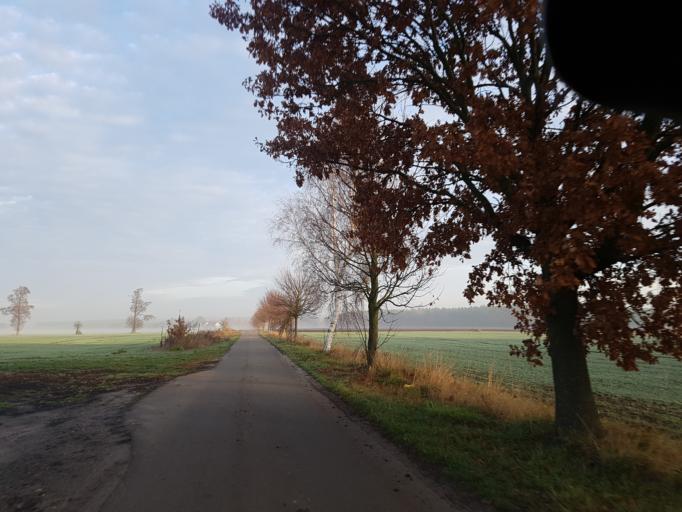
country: DE
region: Saxony-Anhalt
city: Elster
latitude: 51.8707
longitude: 12.8470
